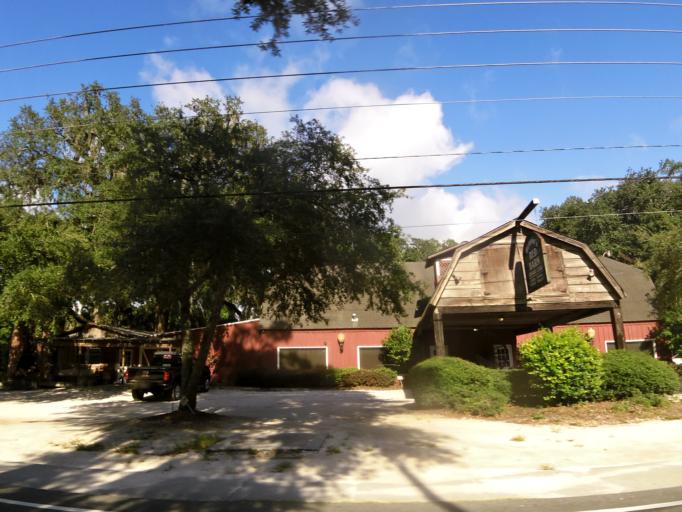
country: US
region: Georgia
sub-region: Glynn County
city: Saint Simon Mills
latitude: 31.2073
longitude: -81.3757
